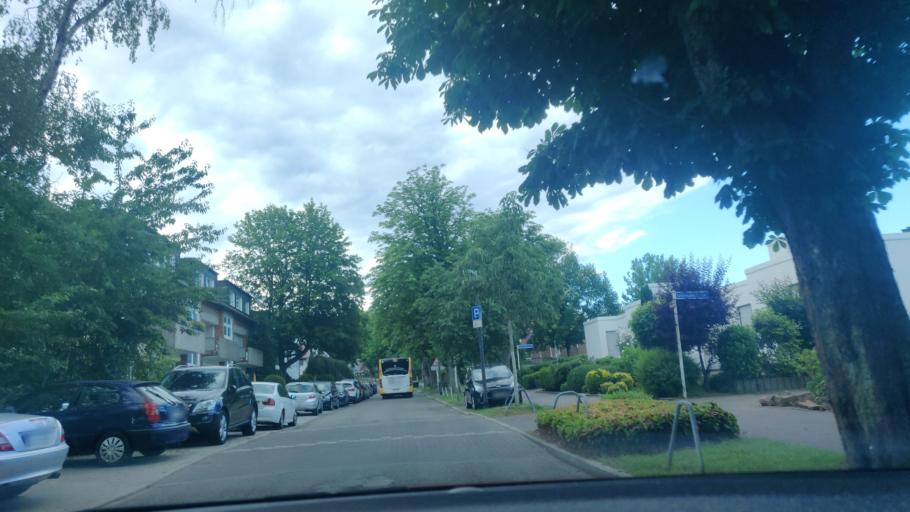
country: DE
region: North Rhine-Westphalia
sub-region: Regierungsbezirk Dusseldorf
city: Velbert
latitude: 51.3763
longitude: 7.0136
